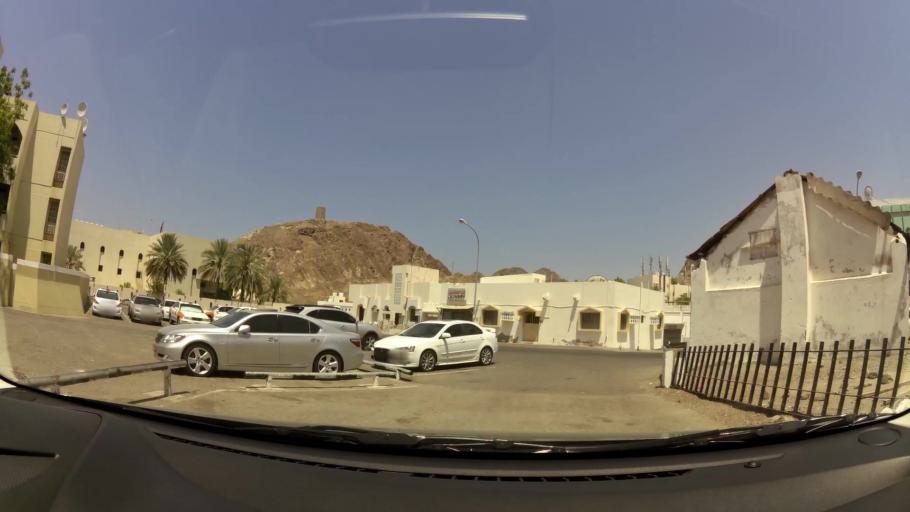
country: OM
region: Muhafazat Masqat
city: Muscat
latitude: 23.6116
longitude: 58.5874
